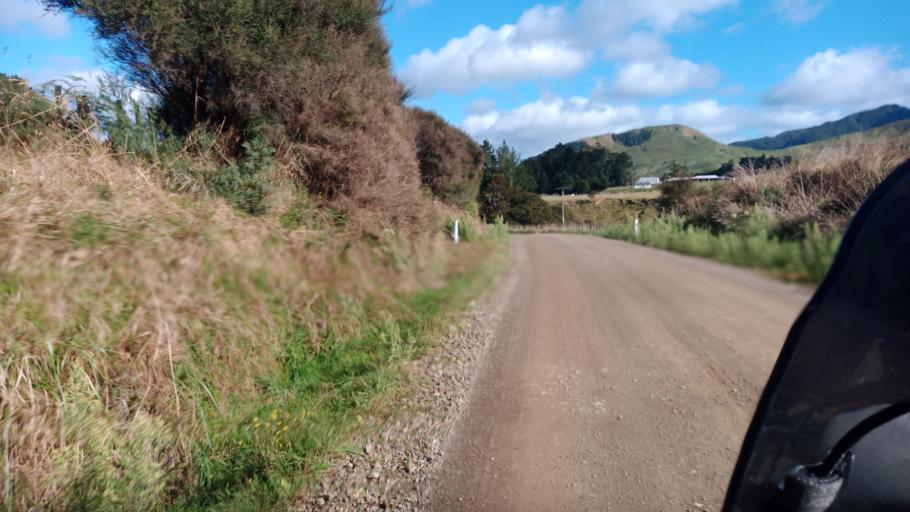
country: NZ
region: Bay of Plenty
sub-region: Opotiki District
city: Opotiki
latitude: -38.4578
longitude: 177.4151
